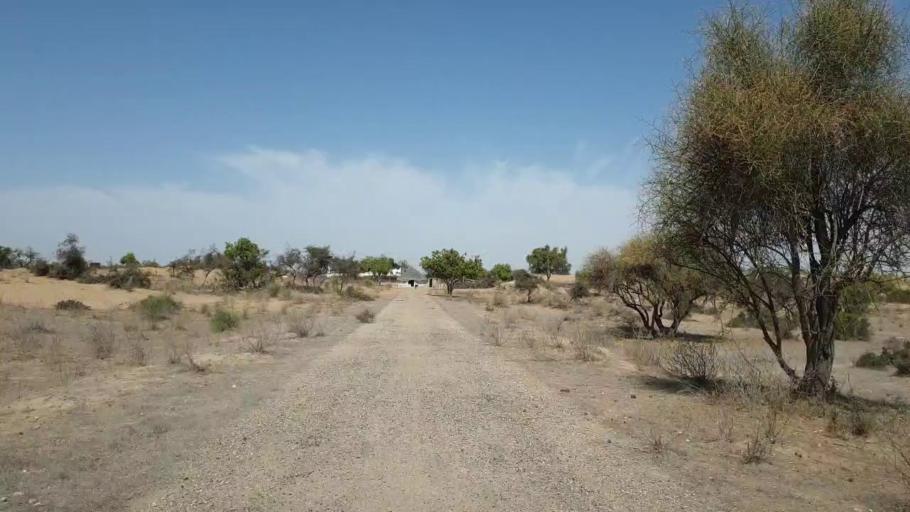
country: PK
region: Sindh
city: Nabisar
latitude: 25.0925
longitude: 69.9904
